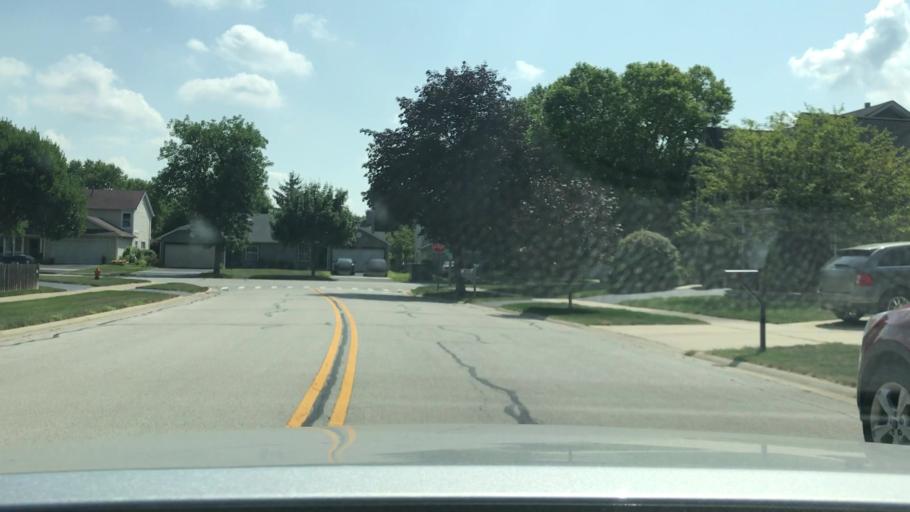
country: US
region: Illinois
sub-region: DuPage County
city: Woodridge
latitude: 41.7429
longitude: -88.0969
